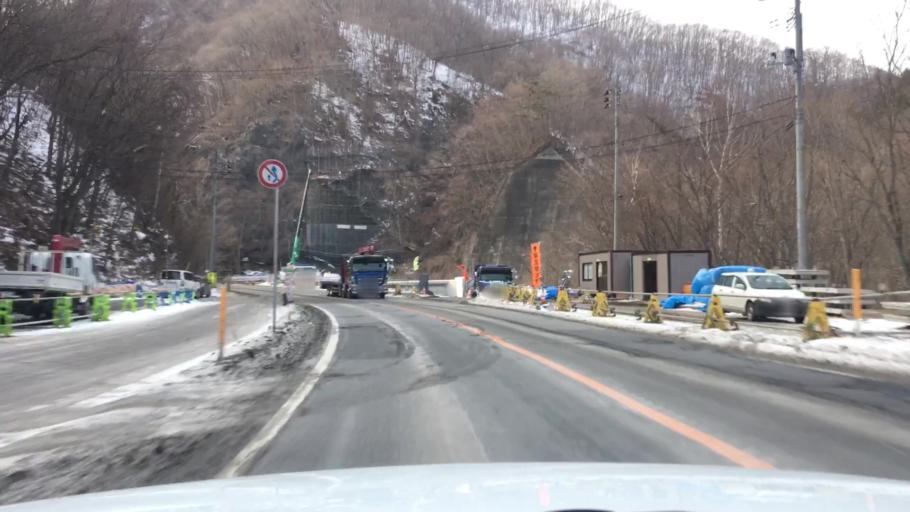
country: JP
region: Iwate
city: Tono
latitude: 39.6316
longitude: 141.5249
